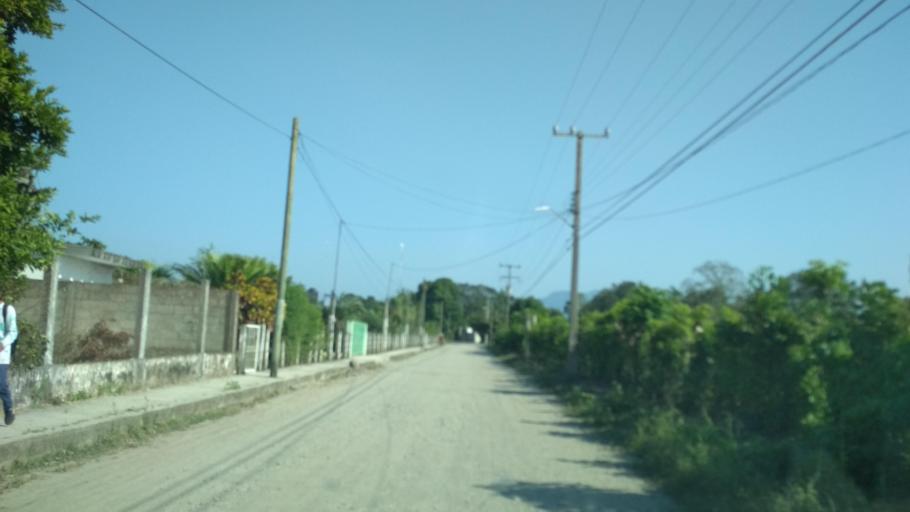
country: MX
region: Veracruz
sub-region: Martinez de la Torre
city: El Progreso
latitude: 20.0815
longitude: -97.0212
